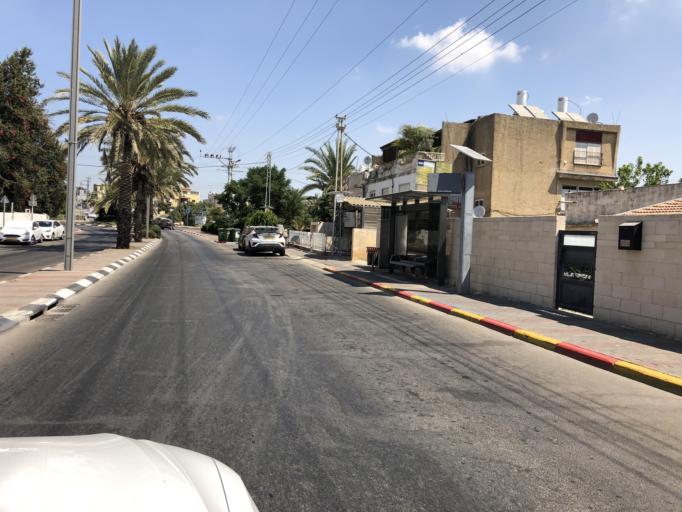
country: IL
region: Central District
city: Rosh Ha'Ayin
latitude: 32.0997
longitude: 34.9549
